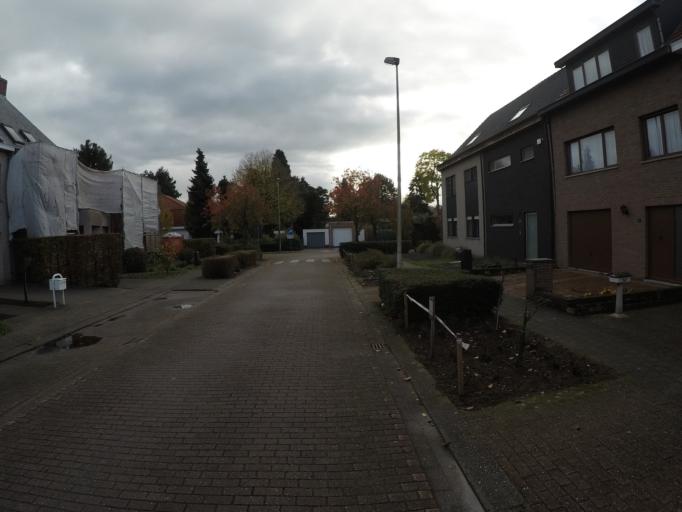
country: BE
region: Flanders
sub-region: Provincie Antwerpen
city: Wijnegem
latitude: 51.2237
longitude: 4.5080
